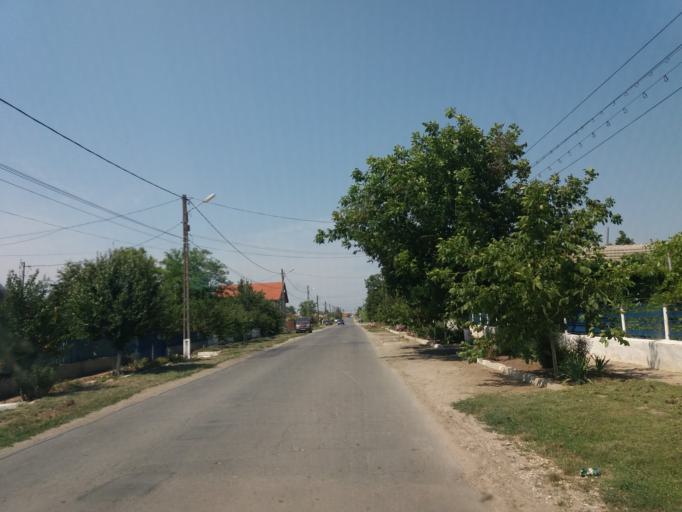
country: RO
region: Constanta
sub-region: Comuna Corbu
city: Corbu
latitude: 44.4005
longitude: 28.6617
